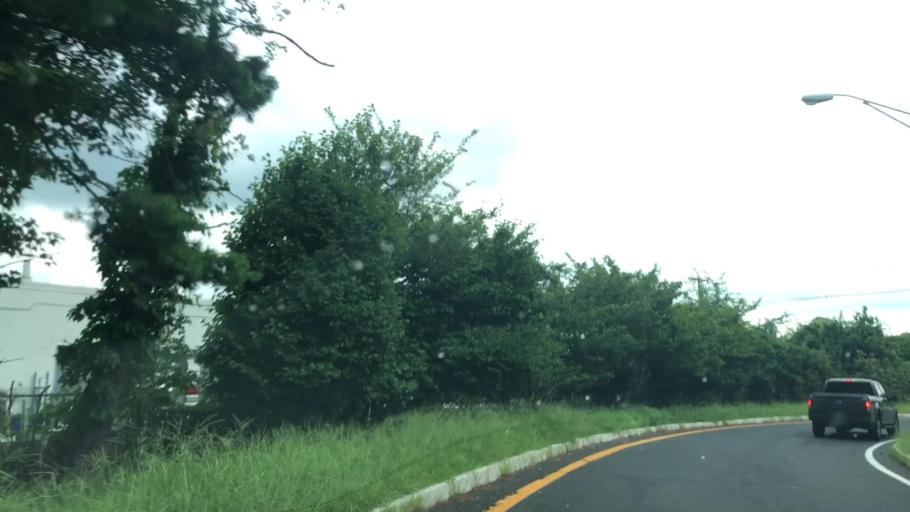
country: US
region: New Jersey
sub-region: Passaic County
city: Totowa
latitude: 40.8986
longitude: -74.2219
